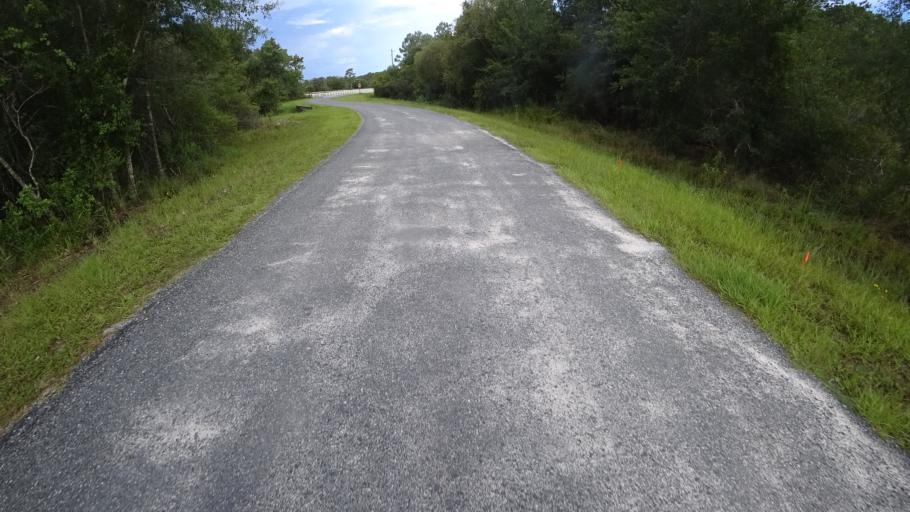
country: US
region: Florida
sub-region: Sarasota County
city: Lake Sarasota
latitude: 27.3981
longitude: -82.2824
